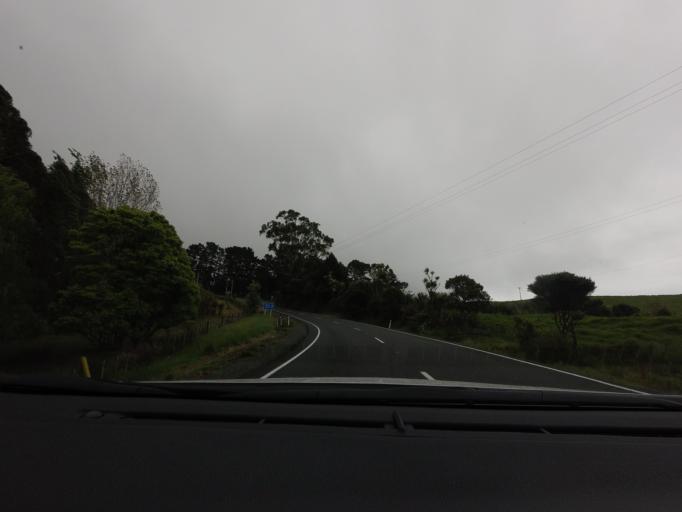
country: NZ
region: Auckland
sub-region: Auckland
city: Warkworth
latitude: -36.2819
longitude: 174.7927
